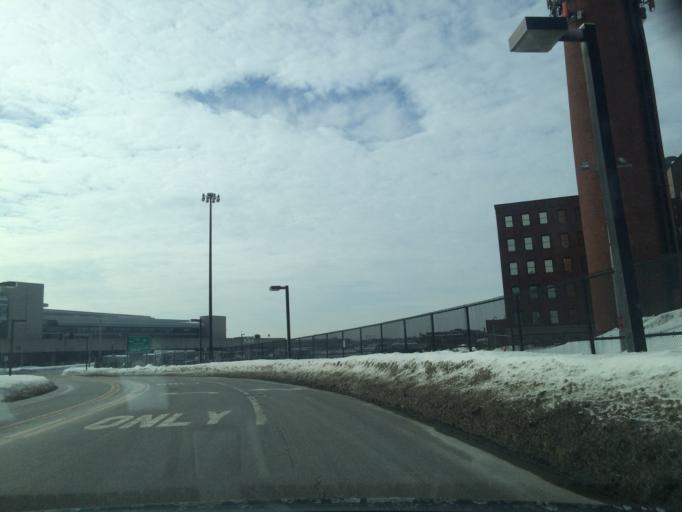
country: US
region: Massachusetts
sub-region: Suffolk County
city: South Boston
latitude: 42.3474
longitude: -71.0488
